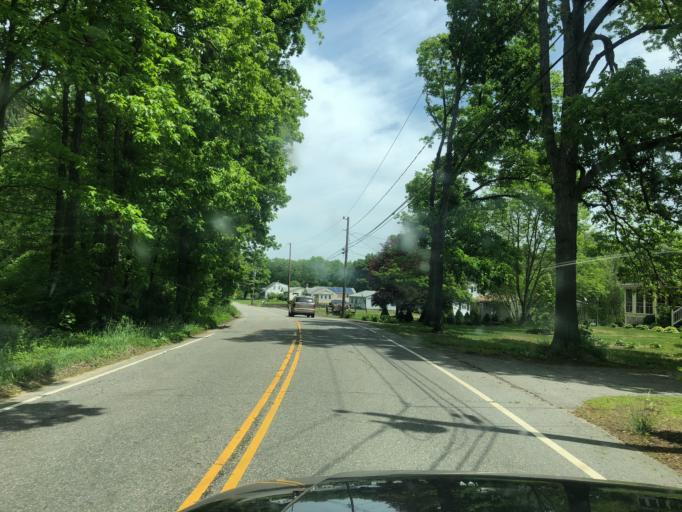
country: US
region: Connecticut
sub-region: Windham County
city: Quinebaug
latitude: 42.0178
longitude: -71.9581
